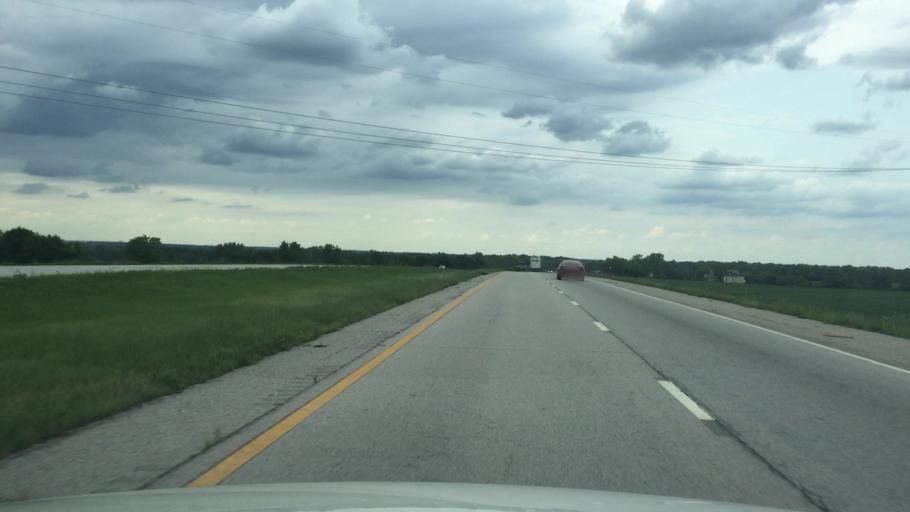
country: US
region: Kansas
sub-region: Miami County
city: Louisburg
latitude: 38.7459
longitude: -94.6768
